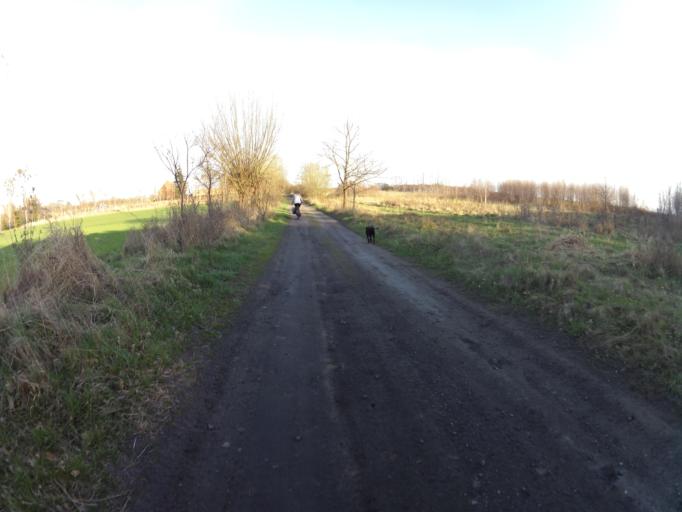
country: PL
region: West Pomeranian Voivodeship
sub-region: Powiat pyrzycki
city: Lipiany
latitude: 52.9546
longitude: 14.9321
